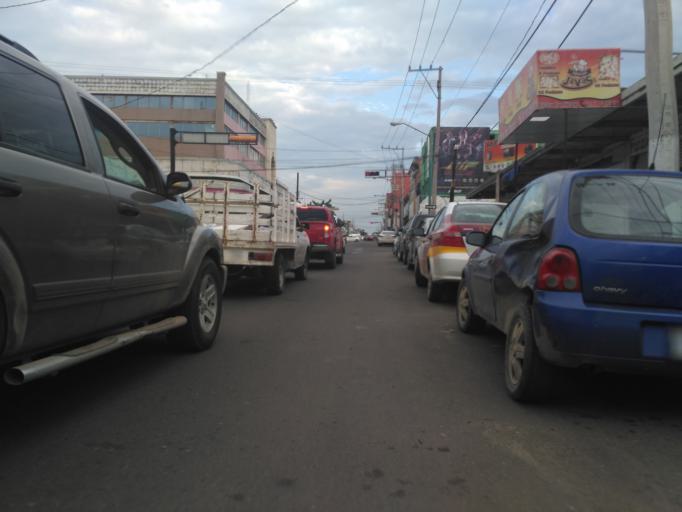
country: MX
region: Sinaloa
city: Culiacan
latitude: 24.8036
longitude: -107.3963
